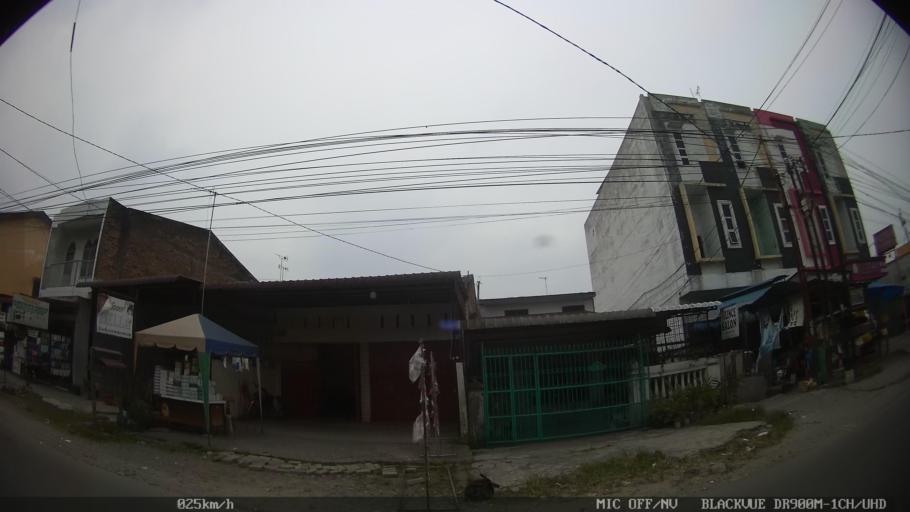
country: ID
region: North Sumatra
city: Medan
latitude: 3.5628
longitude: 98.7020
